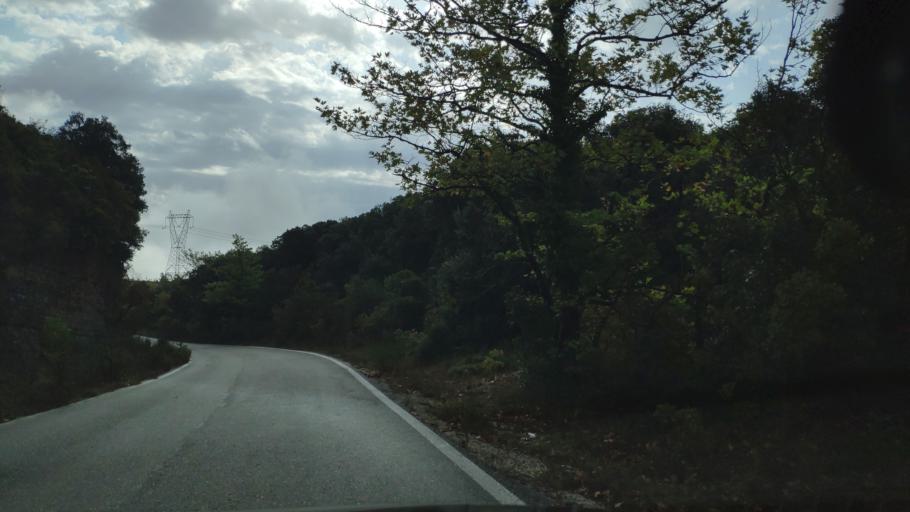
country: GR
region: West Greece
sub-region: Nomos Aitolias kai Akarnanias
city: Sardinia
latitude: 38.8760
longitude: 21.2698
